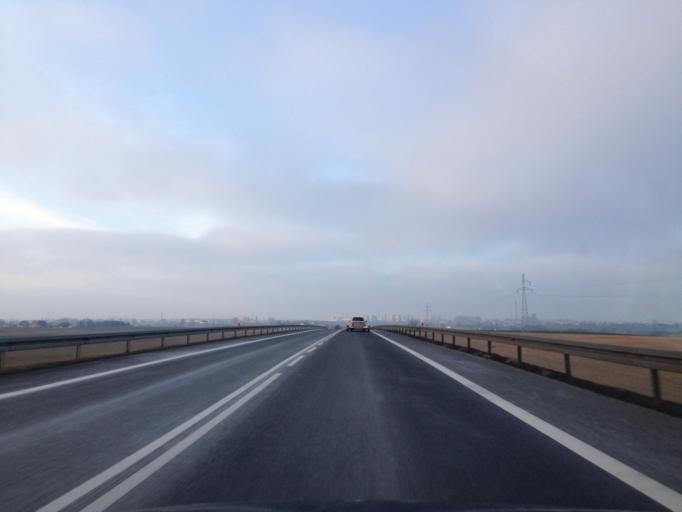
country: PL
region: Greater Poland Voivodeship
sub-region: Powiat gnieznienski
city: Gniezno
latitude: 52.5537
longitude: 17.6581
